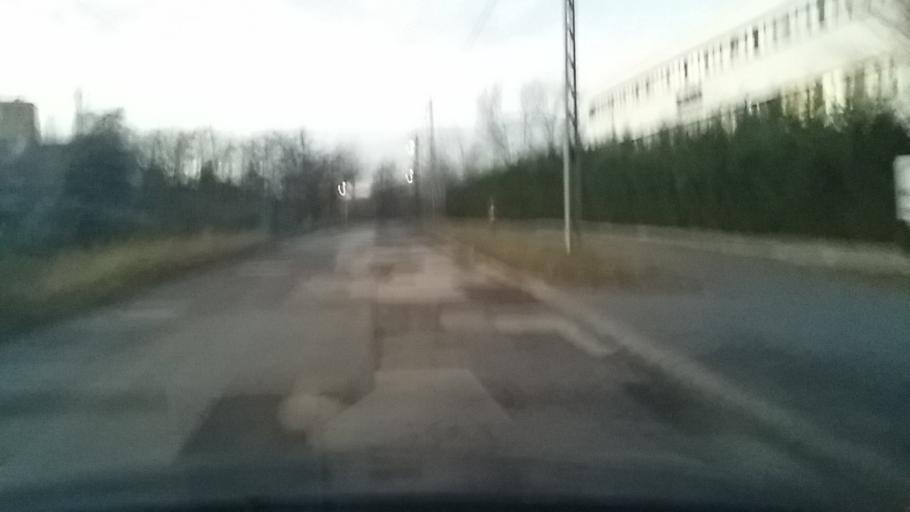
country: HU
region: Budapest
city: Budapest XV. keruelet
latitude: 47.5699
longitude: 19.1302
